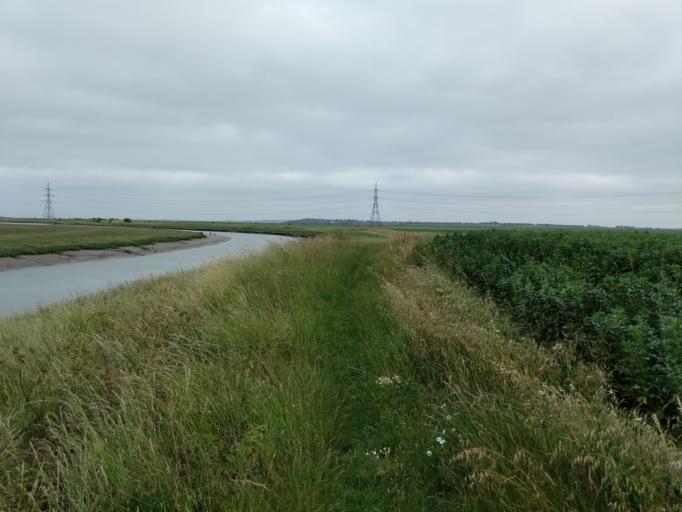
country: GB
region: England
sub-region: Kent
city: Faversham
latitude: 51.3332
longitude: 0.9127
